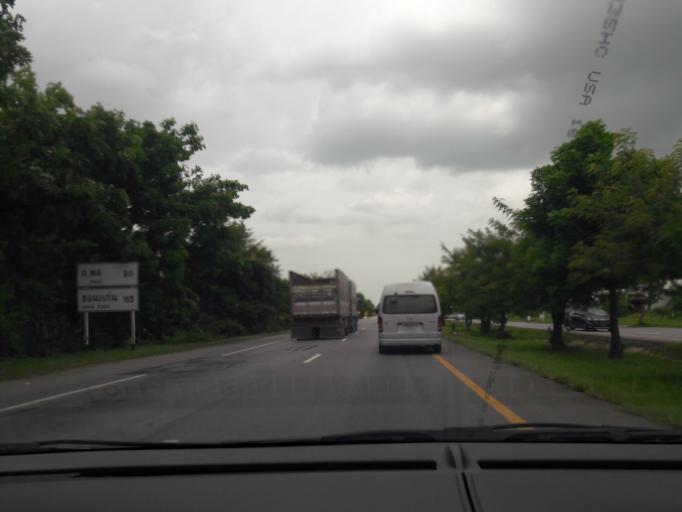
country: TH
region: Nakhon Ratchasima
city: Non Sung
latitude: 15.0975
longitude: 102.2728
